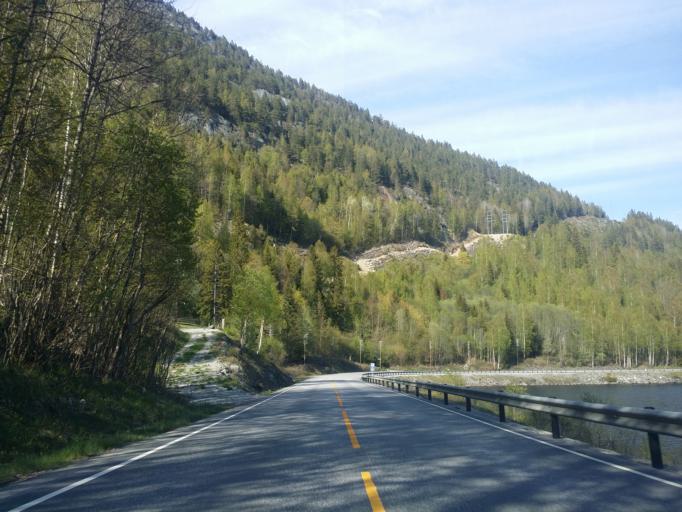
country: NO
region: Telemark
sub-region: Seljord
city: Seljord
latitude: 59.6091
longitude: 8.7504
